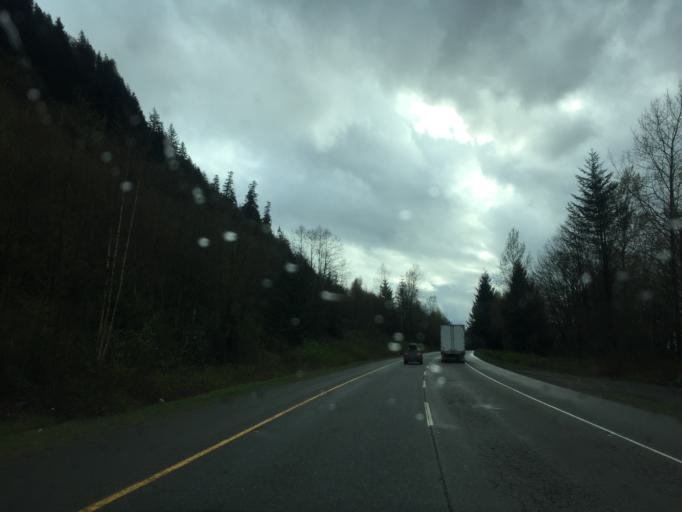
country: CA
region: British Columbia
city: Agassiz
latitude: 49.2754
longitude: -121.6724
